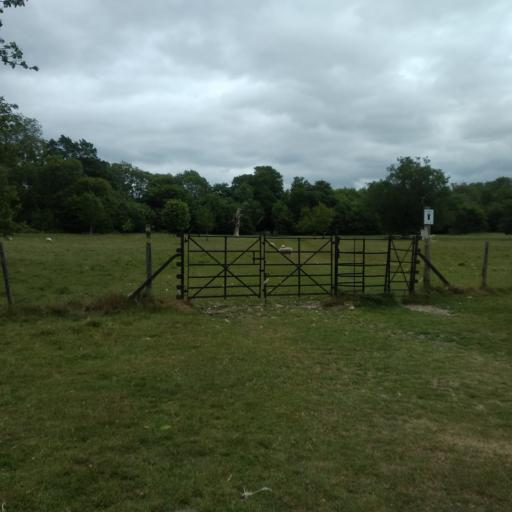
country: GB
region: England
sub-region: Kent
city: Ashford
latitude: 51.1618
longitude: 0.8410
